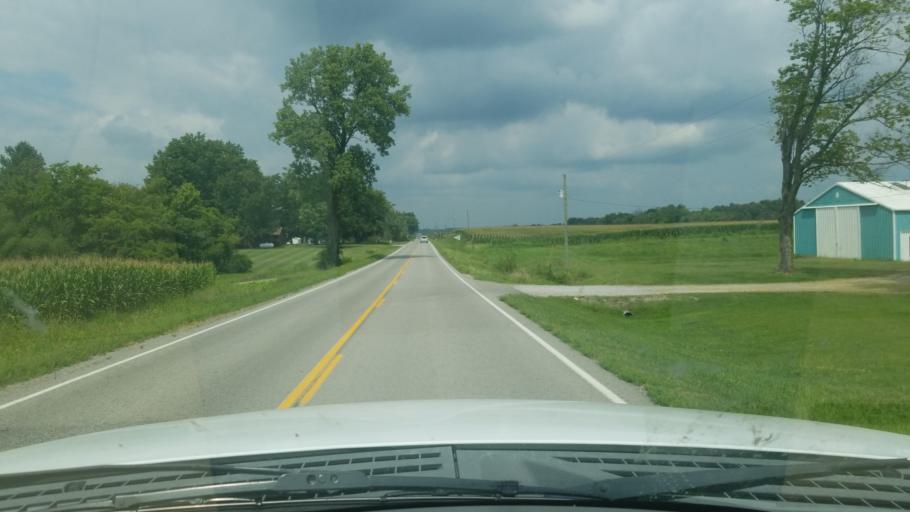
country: US
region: Illinois
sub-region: Saline County
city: Carrier Mills
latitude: 37.8000
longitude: -88.6517
